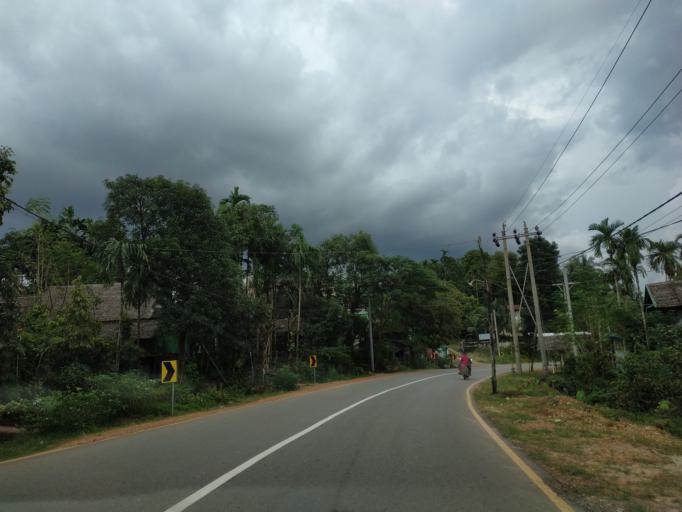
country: MM
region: Tanintharyi
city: Dawei
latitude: 13.9567
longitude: 98.2447
